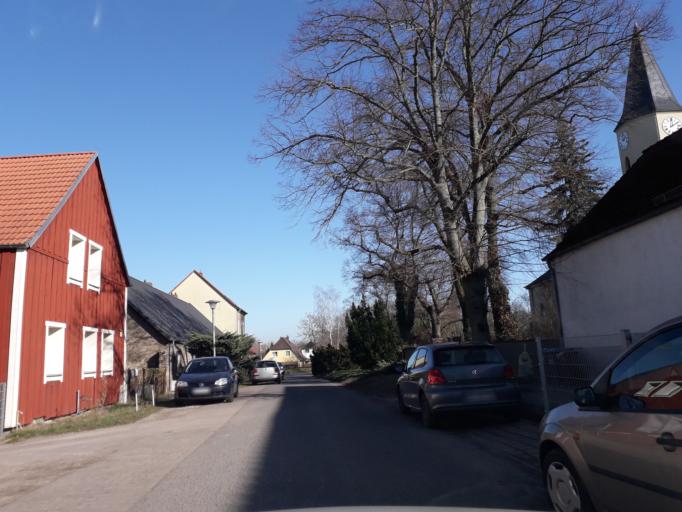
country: DE
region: Brandenburg
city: Wustermark
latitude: 52.5716
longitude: 12.9585
